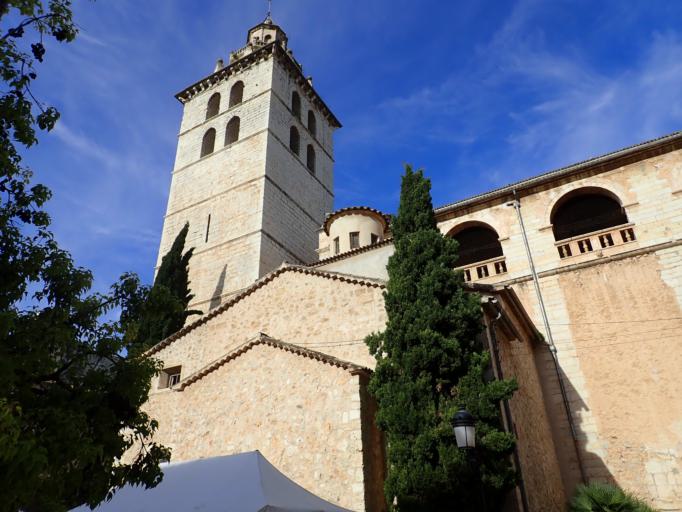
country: ES
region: Balearic Islands
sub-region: Illes Balears
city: Inca
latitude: 39.7213
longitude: 2.9119
